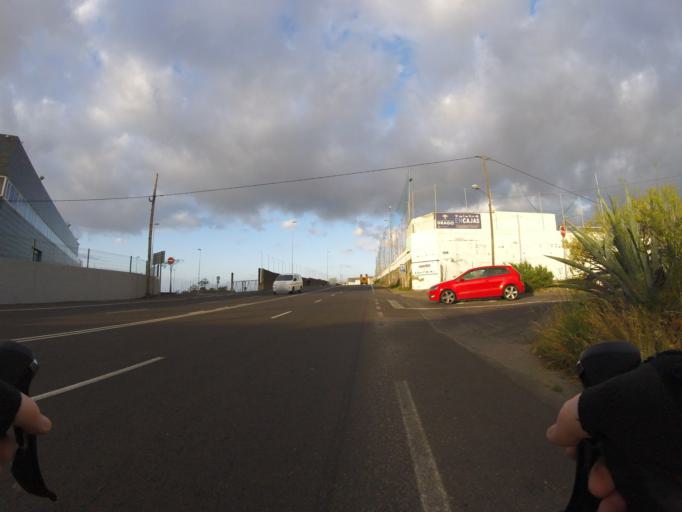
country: ES
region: Canary Islands
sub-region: Provincia de Santa Cruz de Tenerife
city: La Laguna
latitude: 28.4225
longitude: -16.3193
